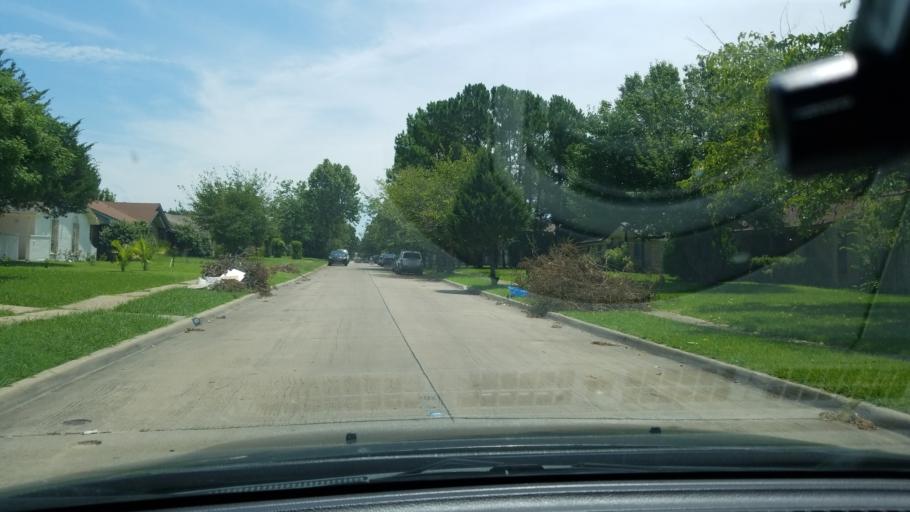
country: US
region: Texas
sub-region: Dallas County
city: Balch Springs
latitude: 32.7408
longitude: -96.6466
